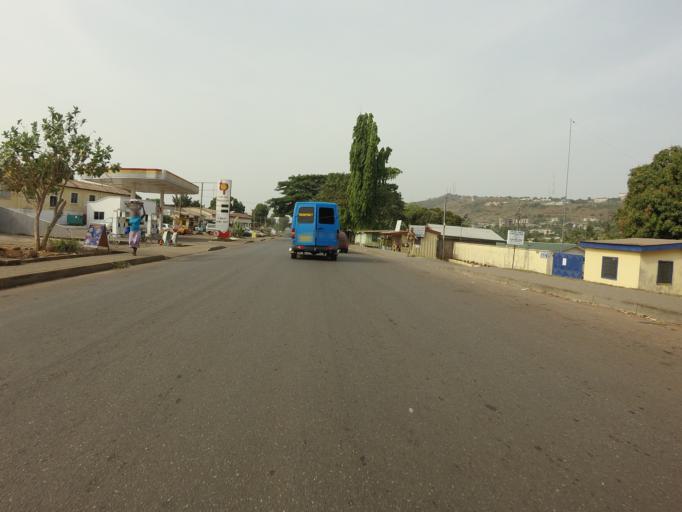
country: GH
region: Volta
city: Ho
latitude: 6.6116
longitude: 0.4612
